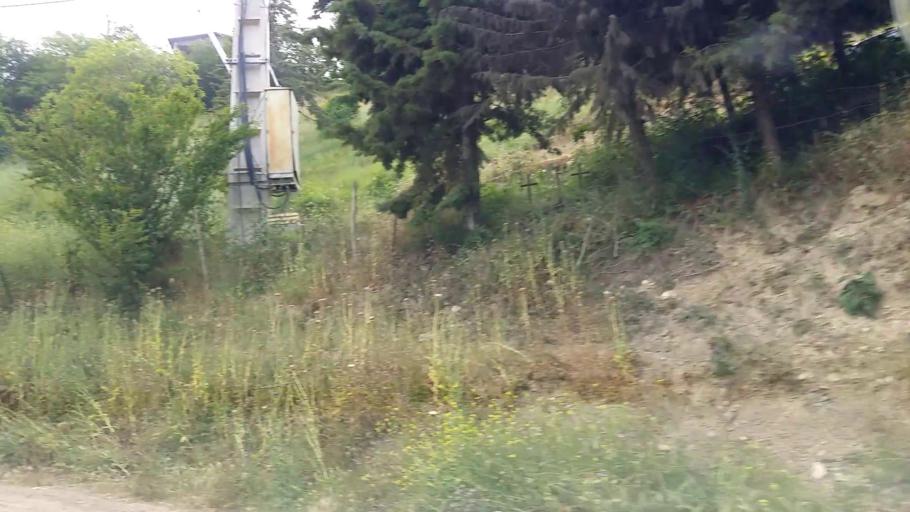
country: IR
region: Mazandaran
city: Chalus
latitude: 36.5555
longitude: 51.2713
